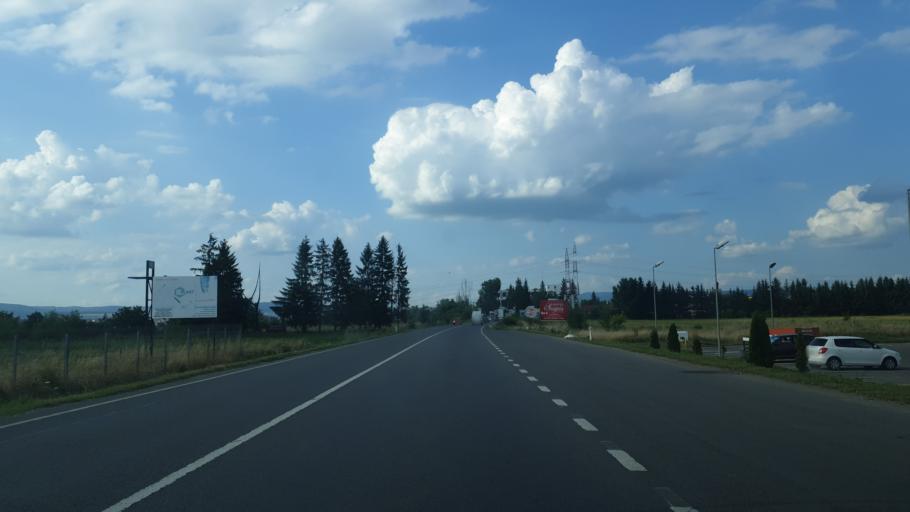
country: RO
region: Covasna
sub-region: Municipiul Sfantu Gheorghe
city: Sfantu-Gheorghe
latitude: 45.8443
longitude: 25.8041
